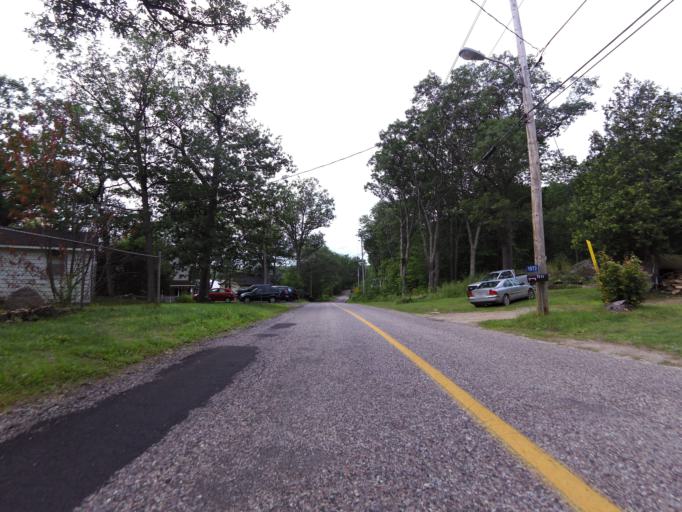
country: CA
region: Ontario
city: Perth
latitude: 44.7307
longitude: -76.6117
